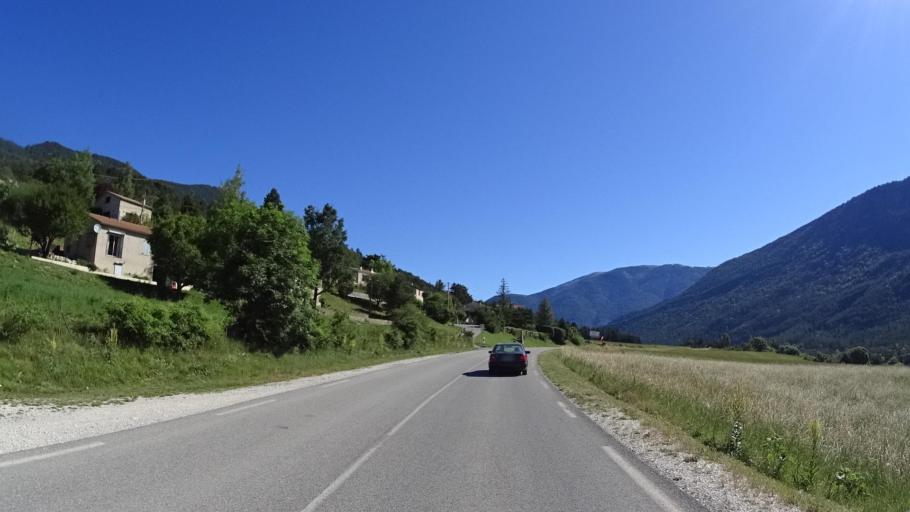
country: FR
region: Provence-Alpes-Cote d'Azur
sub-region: Departement des Alpes-de-Haute-Provence
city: Castellane
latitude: 43.9831
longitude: 6.5270
